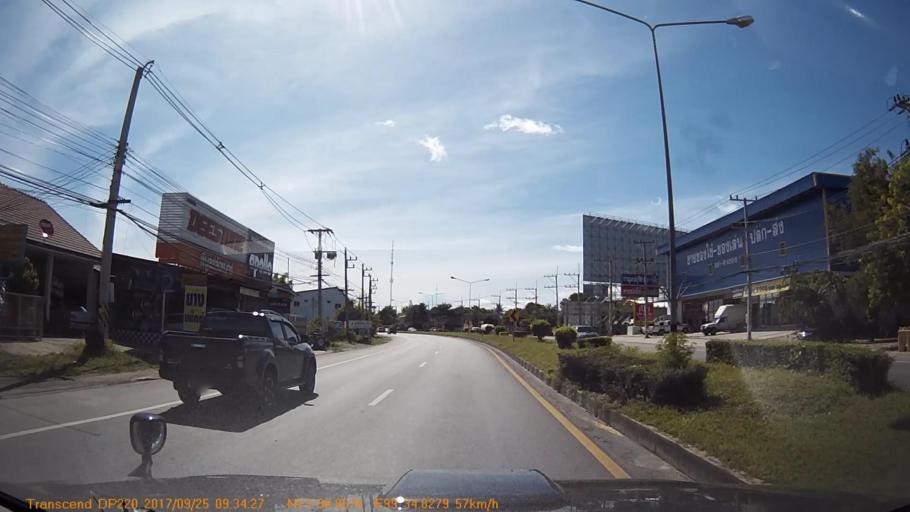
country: TH
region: Kanchanaburi
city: Kanchanaburi
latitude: 13.9809
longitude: 99.5806
